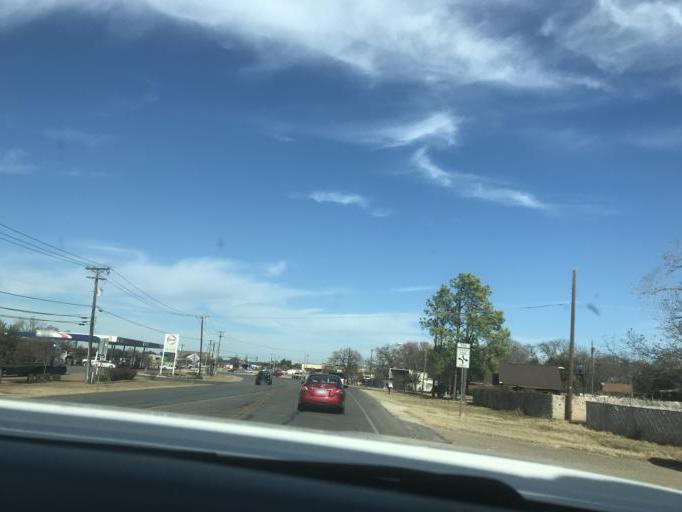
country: US
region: Texas
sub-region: Erath County
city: Stephenville
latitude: 32.2234
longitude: -98.2339
